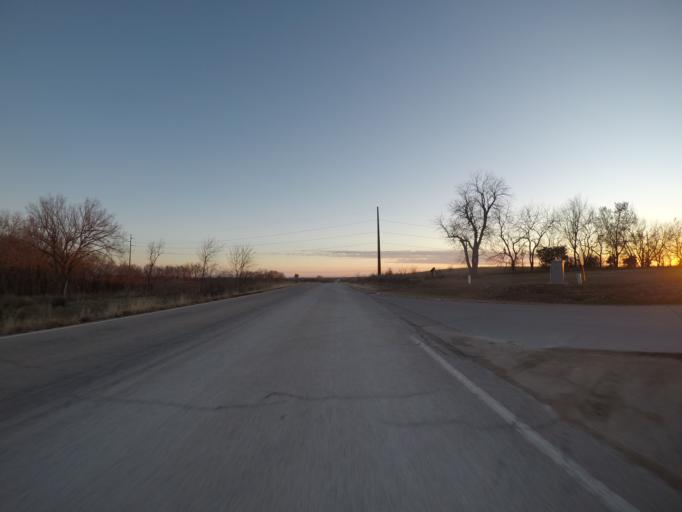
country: US
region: Kansas
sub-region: Riley County
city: Manhattan
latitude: 39.2334
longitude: -96.4827
